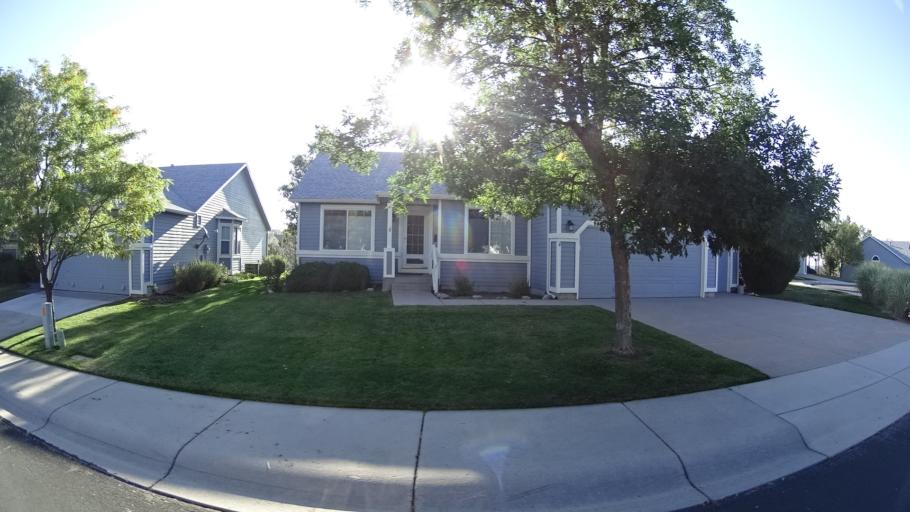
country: US
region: Colorado
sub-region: El Paso County
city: Cimarron Hills
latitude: 38.8910
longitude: -104.7058
